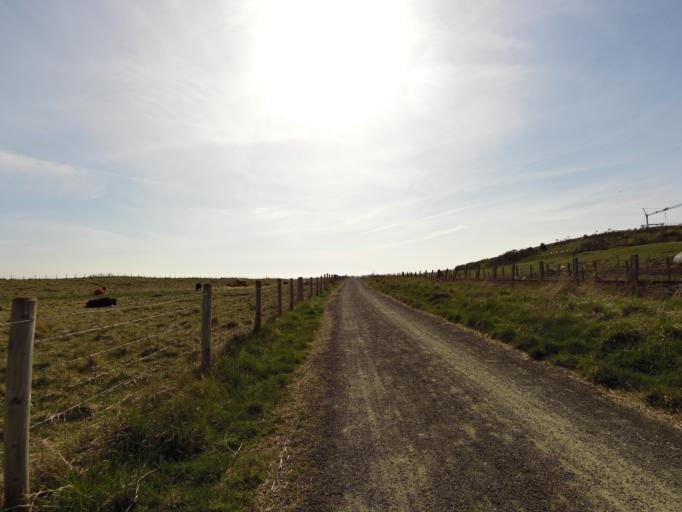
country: GB
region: Scotland
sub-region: Angus
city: Carnoustie
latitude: 56.5257
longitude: -2.6427
